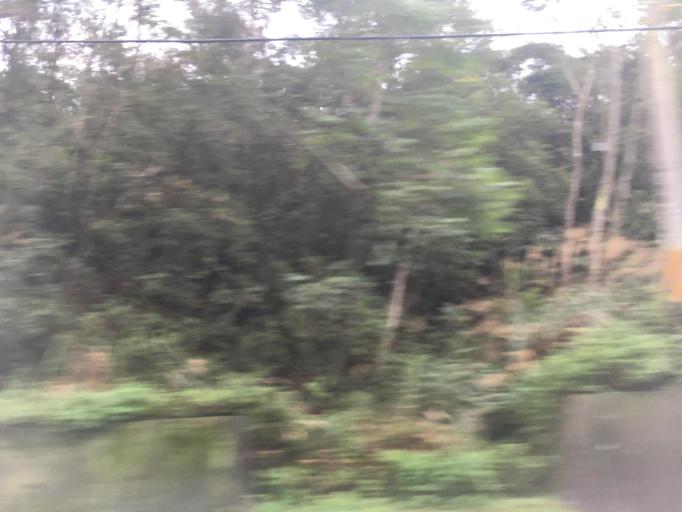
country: TW
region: Taiwan
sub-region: Miaoli
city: Miaoli
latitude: 24.4183
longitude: 120.7575
